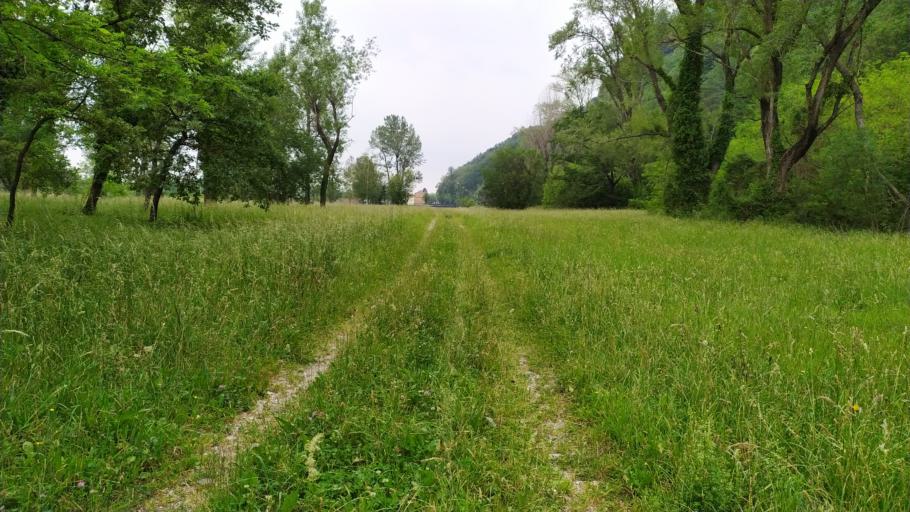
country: IT
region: Friuli Venezia Giulia
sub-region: Provincia di Udine
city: Osoppo
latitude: 46.2630
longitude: 13.0845
